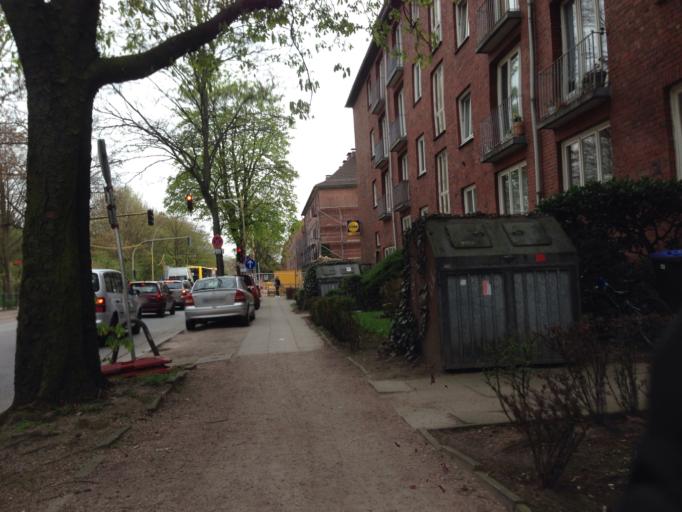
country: DE
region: Hamburg
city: Barmbek-Nord
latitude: 53.5851
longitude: 10.0528
